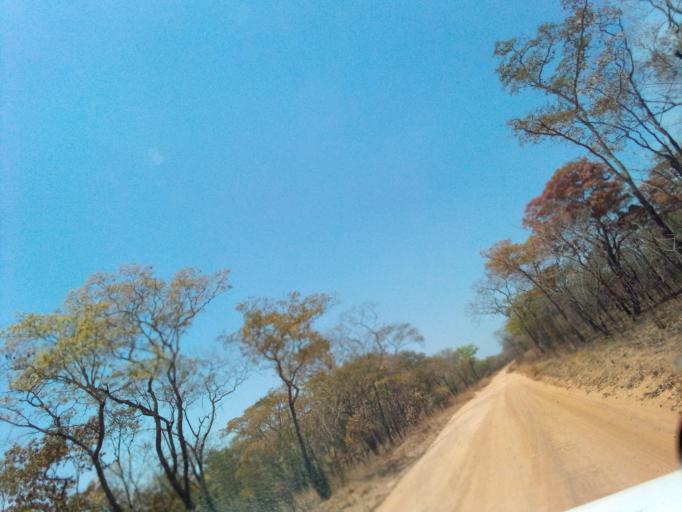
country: ZM
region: Northern
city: Mpika
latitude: -12.2364
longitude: 30.8070
